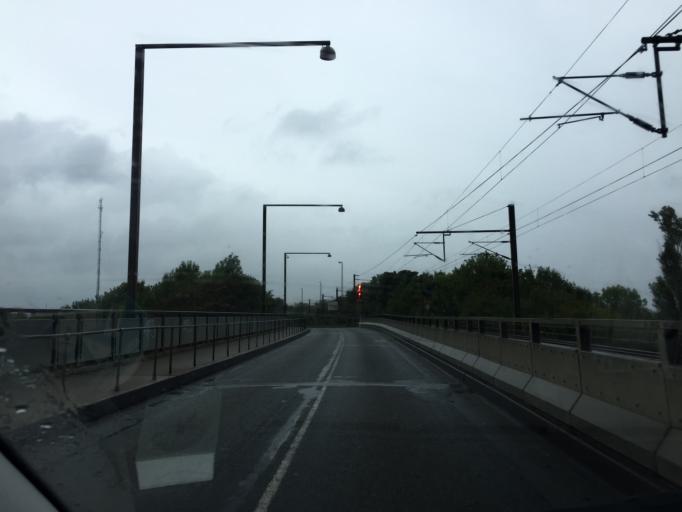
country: DK
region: South Denmark
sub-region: Fredericia Kommune
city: Snoghoj
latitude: 55.5216
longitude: 9.7144
